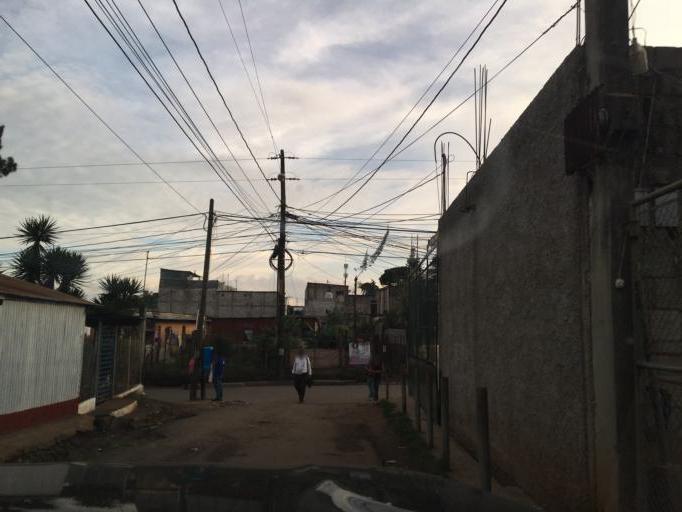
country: GT
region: Guatemala
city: Mixco
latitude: 14.6210
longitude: -90.5793
